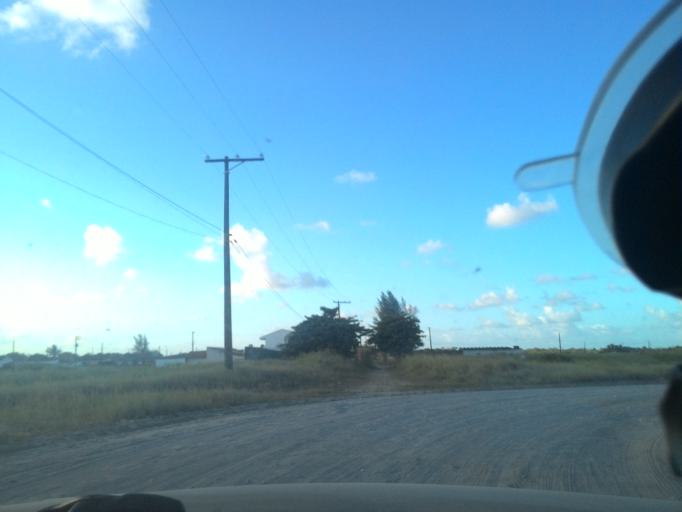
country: BR
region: Sao Paulo
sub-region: Iguape
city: Iguape
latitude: -24.8343
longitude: -47.6740
